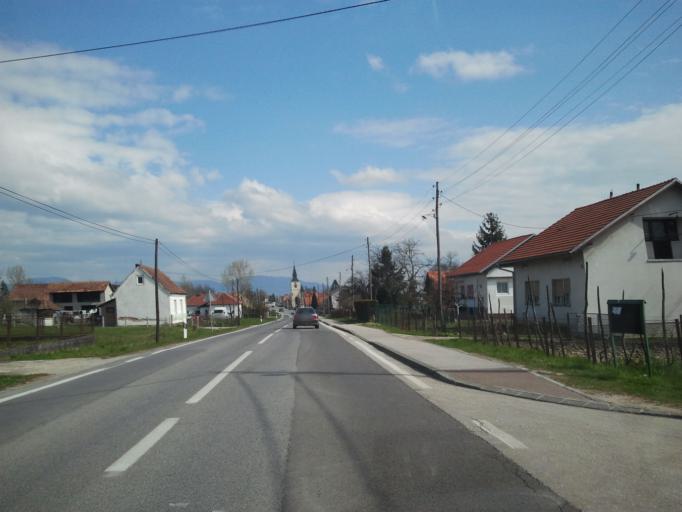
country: HR
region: Zagrebacka
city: Jastrebarsko
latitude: 45.5838
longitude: 15.5946
